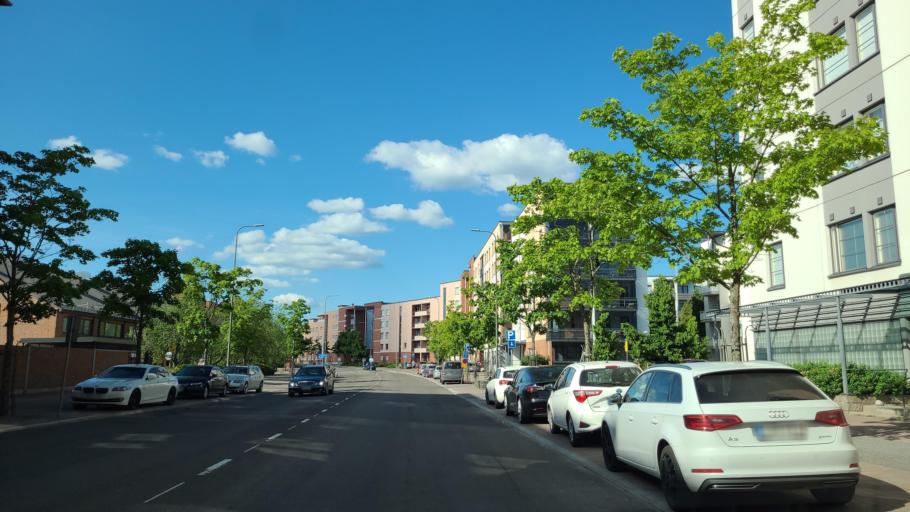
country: FI
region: Central Finland
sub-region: Jyvaeskylae
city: Jyvaeskylae
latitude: 62.2406
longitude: 25.7620
